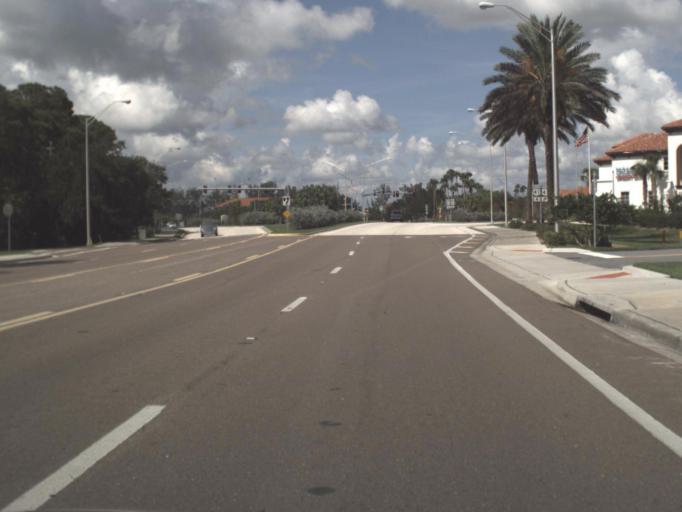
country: US
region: Florida
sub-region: Sarasota County
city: Nokomis
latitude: 27.1072
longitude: -82.4441
